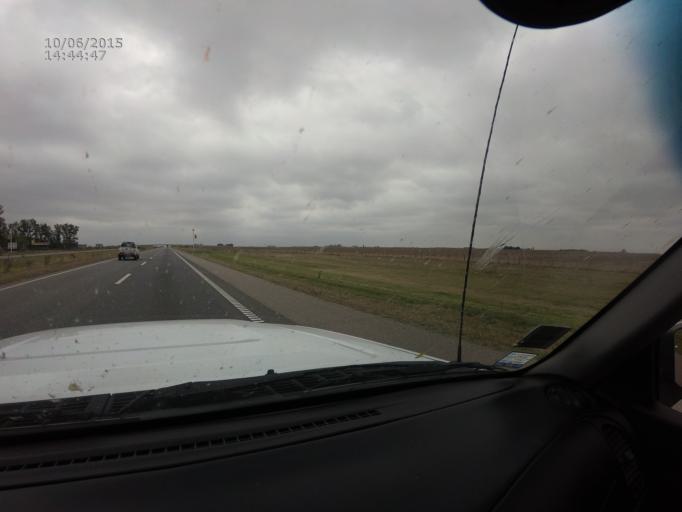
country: AR
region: Cordoba
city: Oliva
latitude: -31.9967
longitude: -63.5566
